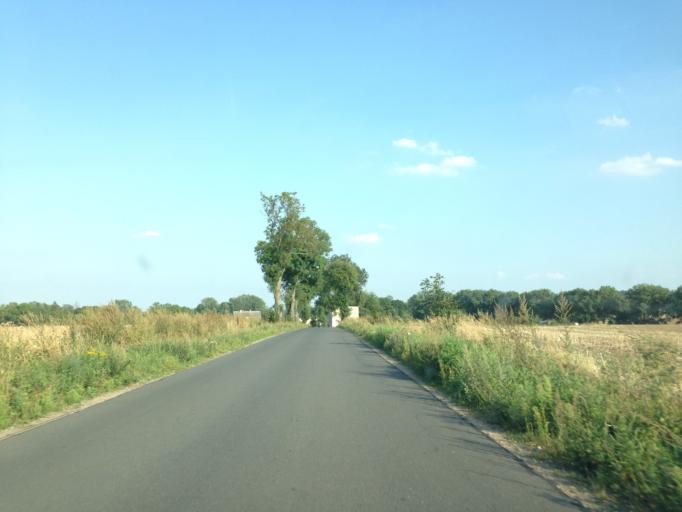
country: PL
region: Warmian-Masurian Voivodeship
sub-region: Powiat nowomiejski
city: Biskupiec
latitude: 53.4174
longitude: 19.3318
